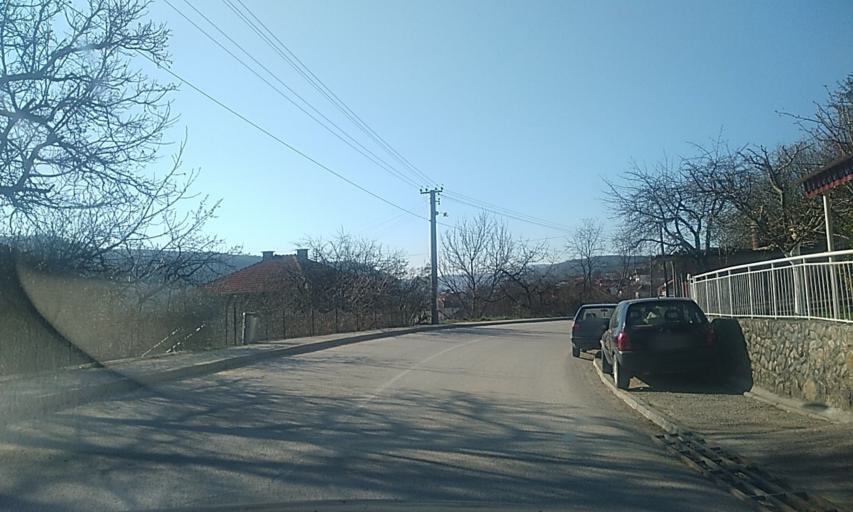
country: RS
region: Central Serbia
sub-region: Pcinjski Okrug
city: Bosilegrad
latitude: 42.4897
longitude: 22.4716
